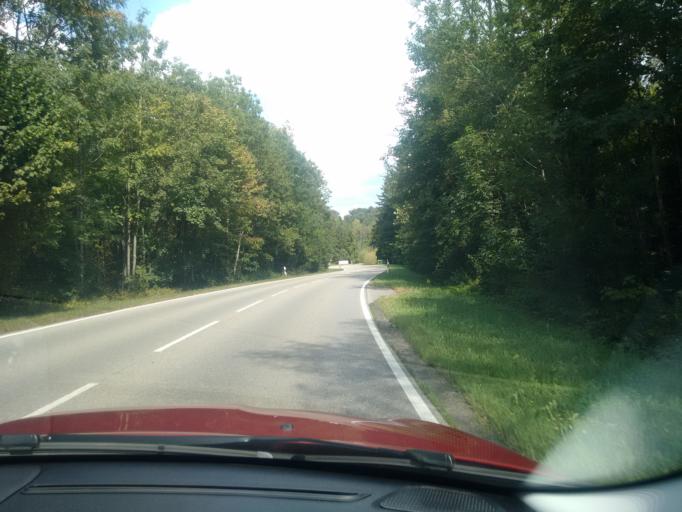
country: DE
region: Bavaria
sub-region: Upper Bavaria
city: Trostberg an der Alz
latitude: 48.0408
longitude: 12.5756
